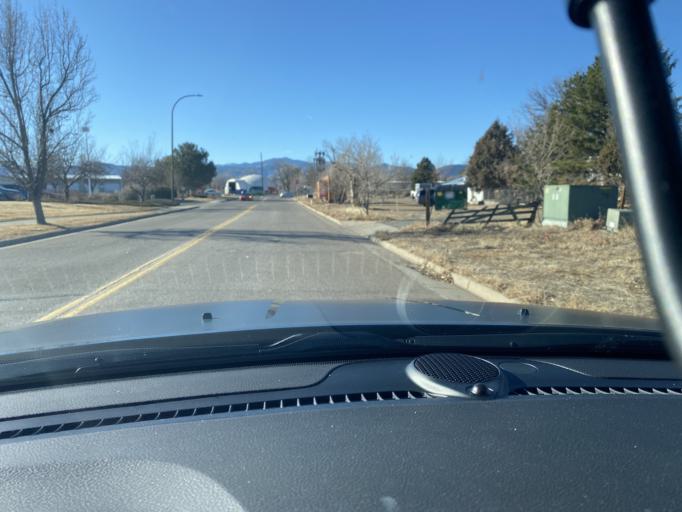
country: US
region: Colorado
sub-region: Jefferson County
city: Applewood
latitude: 39.8152
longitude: -105.1635
